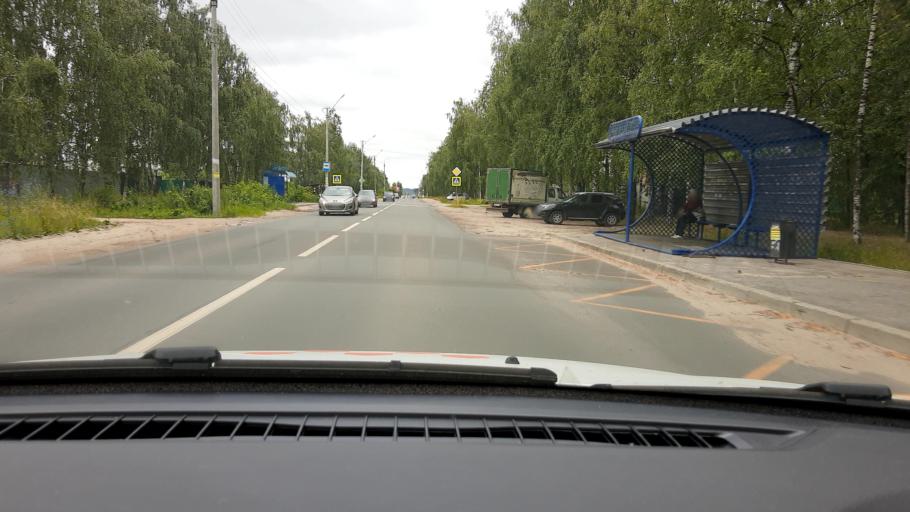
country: RU
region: Nizjnij Novgorod
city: Dzerzhinsk
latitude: 56.2416
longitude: 43.3904
